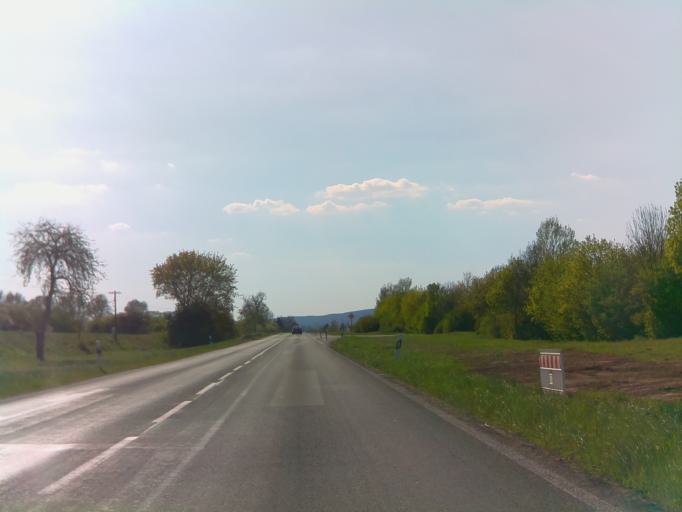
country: DE
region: Thuringia
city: Dreitzsch
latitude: 50.7384
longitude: 11.7829
